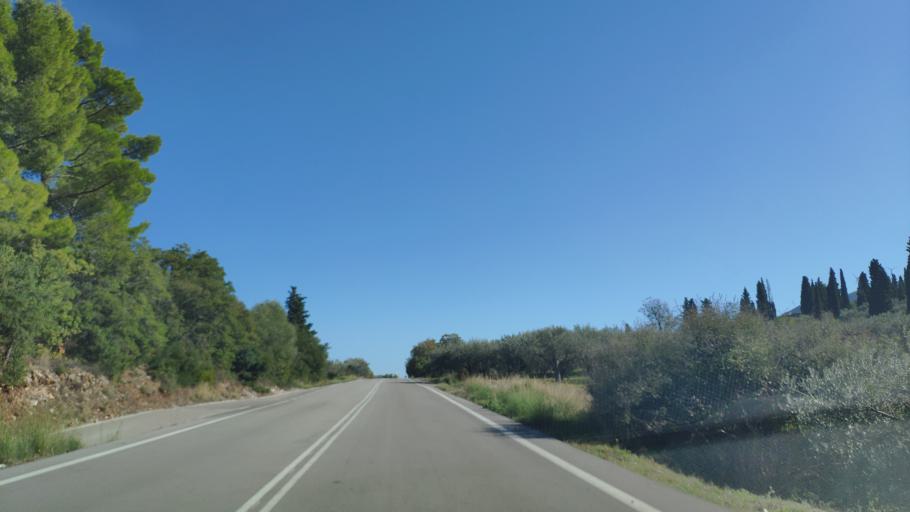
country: GR
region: Peloponnese
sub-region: Nomos Argolidos
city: Palaia Epidavros
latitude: 37.5765
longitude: 23.2441
